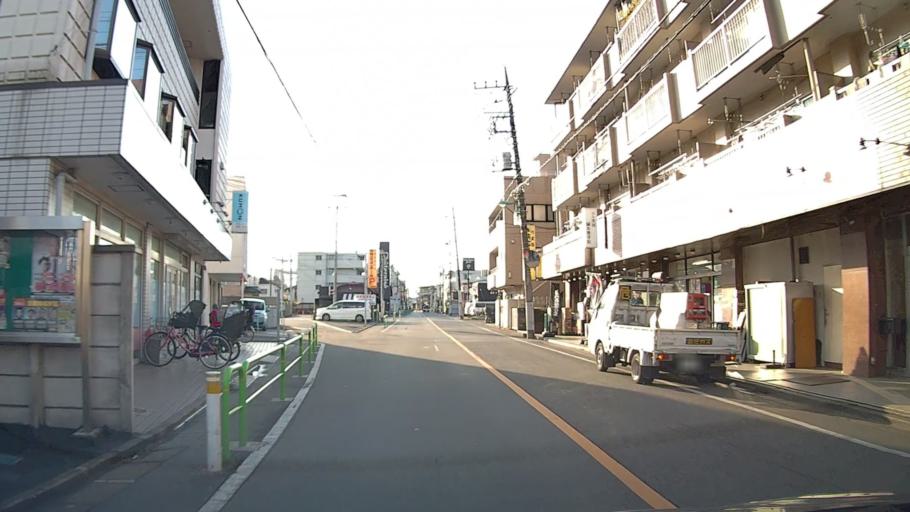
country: JP
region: Saitama
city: Wako
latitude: 35.7664
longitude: 139.6414
